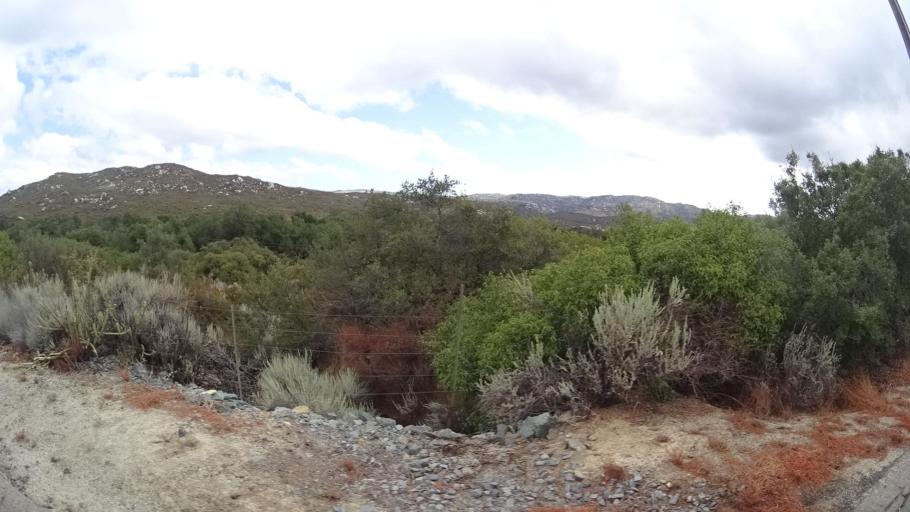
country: US
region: California
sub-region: San Diego County
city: Campo
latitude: 32.6806
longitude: -116.4297
